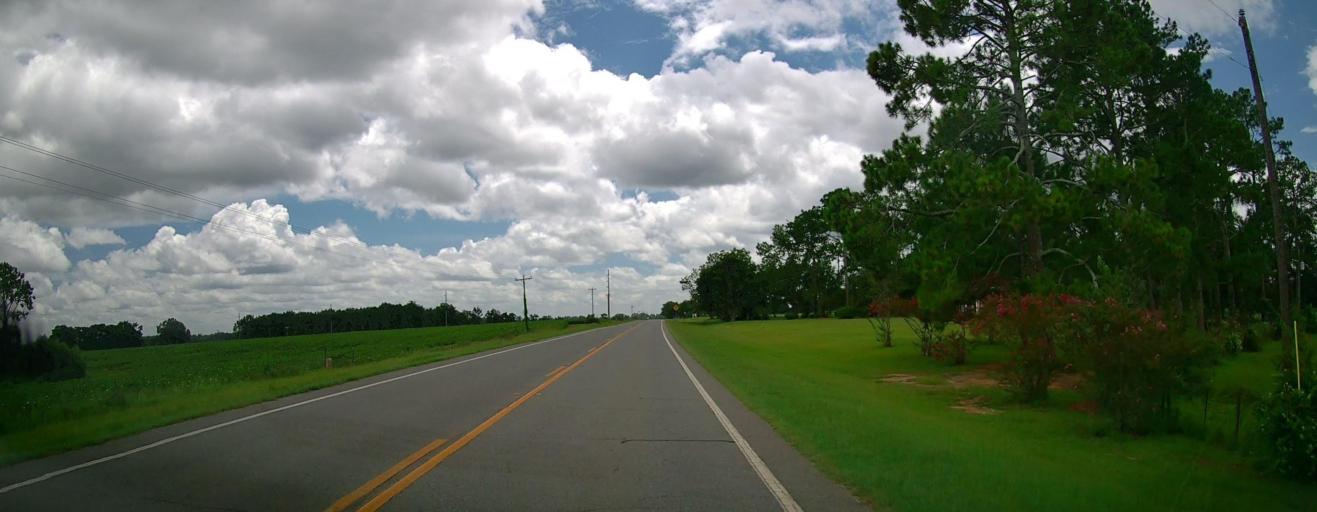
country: US
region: Georgia
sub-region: Wilcox County
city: Rochelle
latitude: 31.9834
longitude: -83.5454
